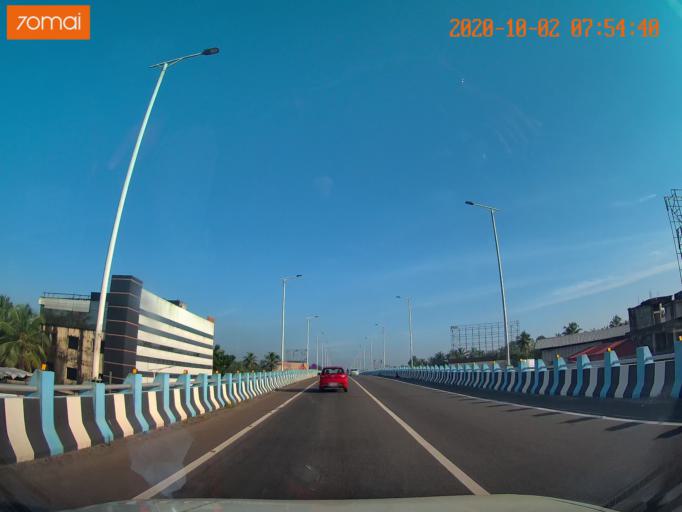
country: IN
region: Kerala
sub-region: Kozhikode
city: Ferokh
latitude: 11.1755
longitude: 75.8739
